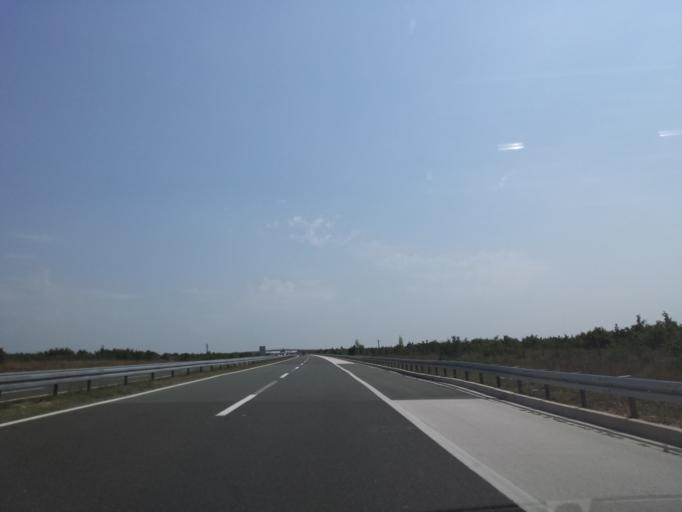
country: HR
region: Sibensko-Kniniska
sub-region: Grad Sibenik
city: Pirovac
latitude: 43.9323
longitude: 15.7128
